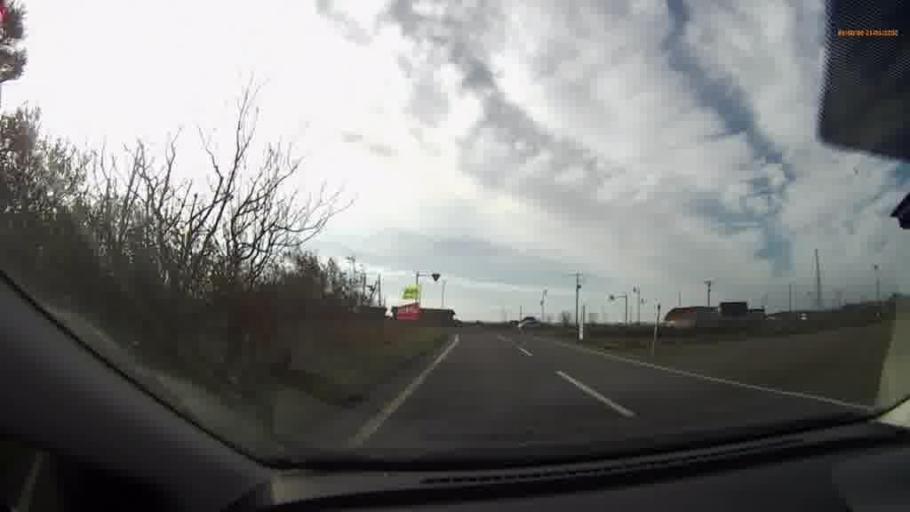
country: JP
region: Hokkaido
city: Kushiro
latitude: 42.8930
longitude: 143.9470
